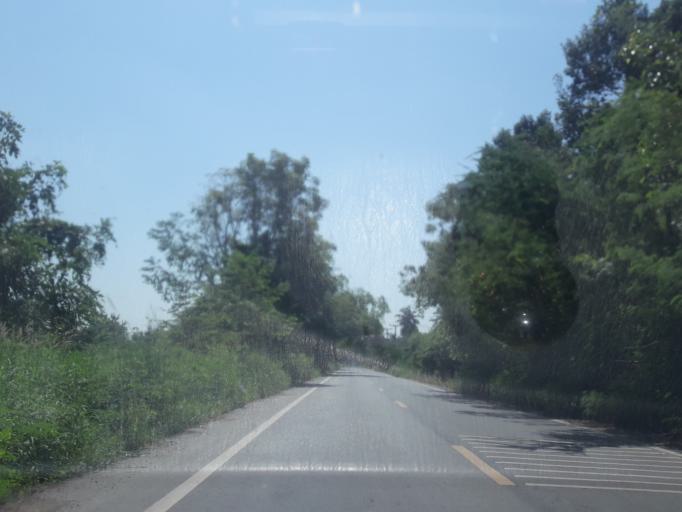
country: TH
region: Pathum Thani
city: Nong Suea
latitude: 14.1046
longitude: 100.8685
